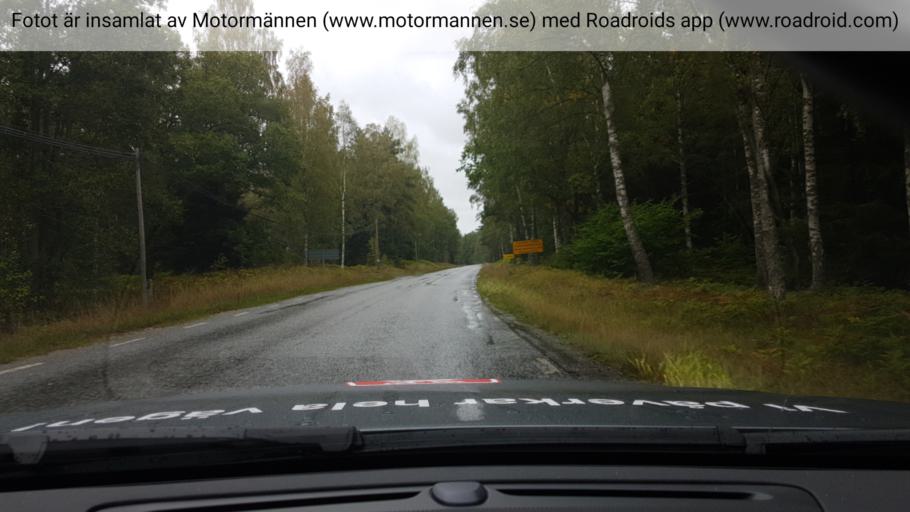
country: SE
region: Stockholm
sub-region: Haninge Kommun
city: Jordbro
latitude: 58.9941
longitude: 18.1013
